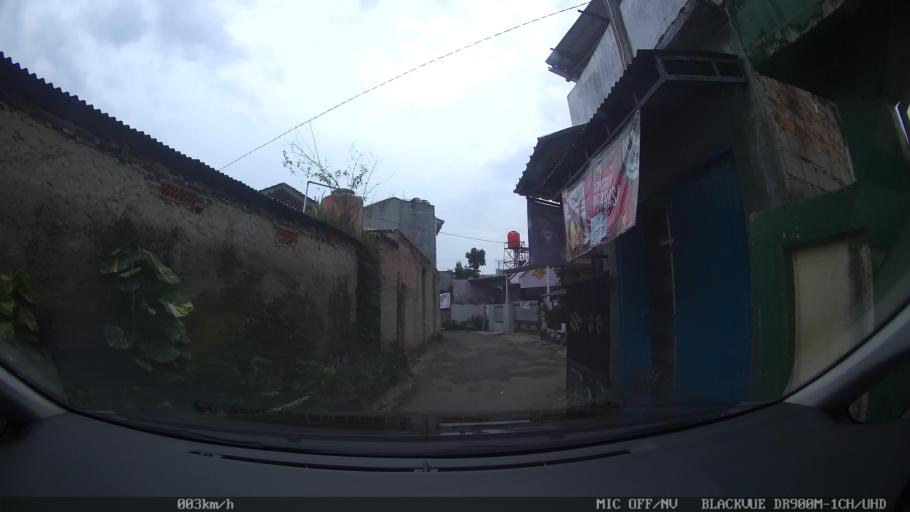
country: ID
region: Lampung
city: Kedaton
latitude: -5.3836
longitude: 105.2550
